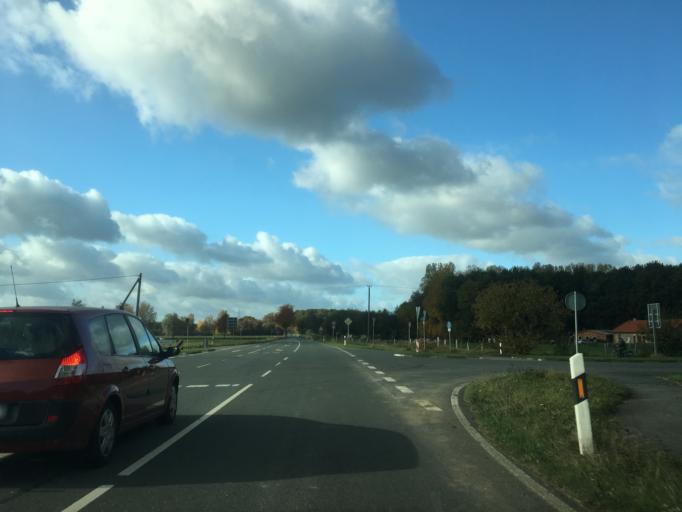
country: DE
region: North Rhine-Westphalia
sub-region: Regierungsbezirk Munster
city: Havixbeck
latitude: 51.9932
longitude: 7.4545
